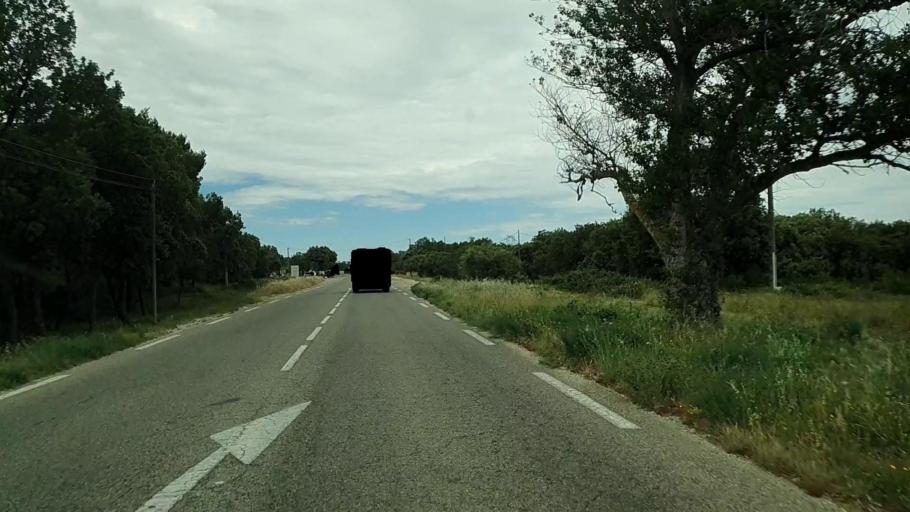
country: FR
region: Languedoc-Roussillon
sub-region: Departement du Gard
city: Connaux
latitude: 44.0516
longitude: 4.5725
